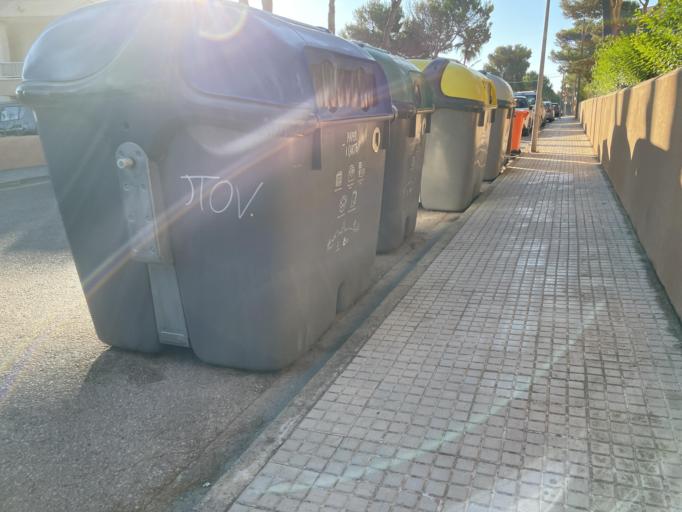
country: ES
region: Balearic Islands
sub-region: Illes Balears
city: Capdepera
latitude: 39.7176
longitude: 3.4556
